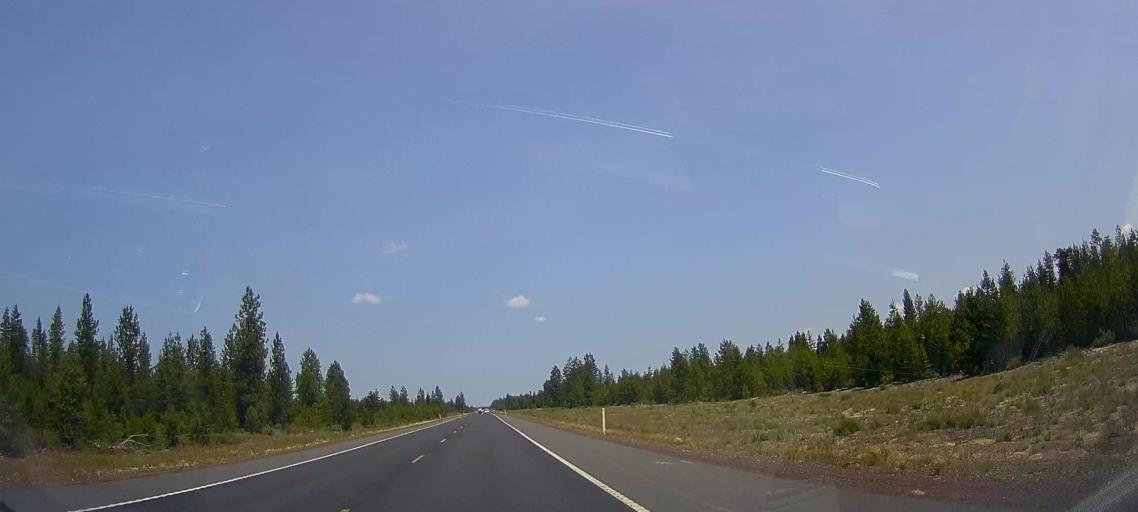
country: US
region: Oregon
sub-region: Deschutes County
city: La Pine
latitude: 43.4978
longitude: -121.6715
